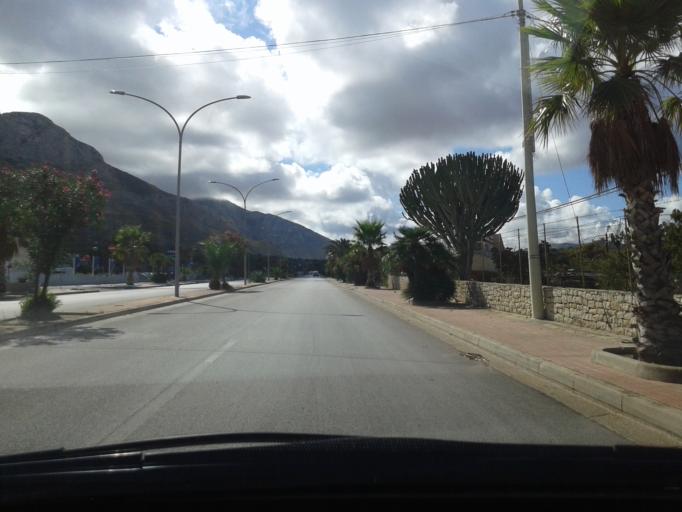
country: IT
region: Sicily
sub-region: Trapani
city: San Vito Lo Capo
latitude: 38.1649
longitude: 12.7356
